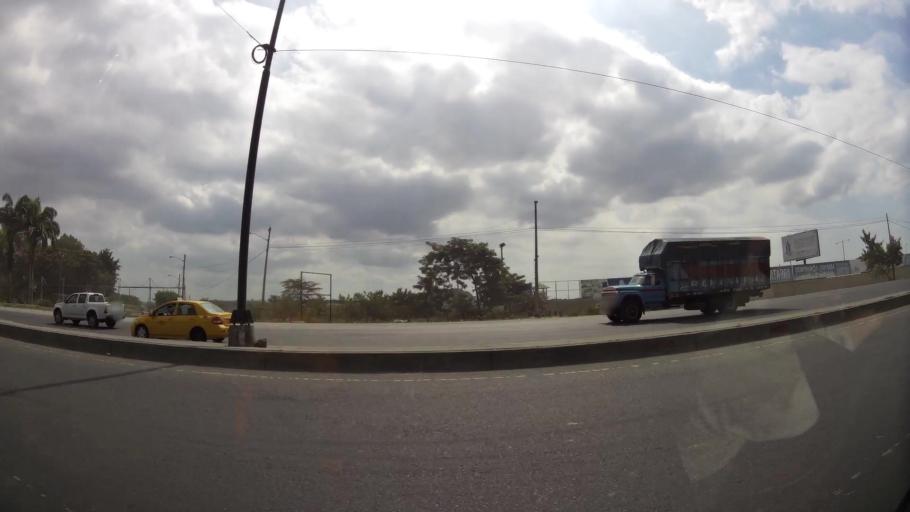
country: EC
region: Guayas
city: Santa Lucia
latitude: -2.0869
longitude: -79.9465
